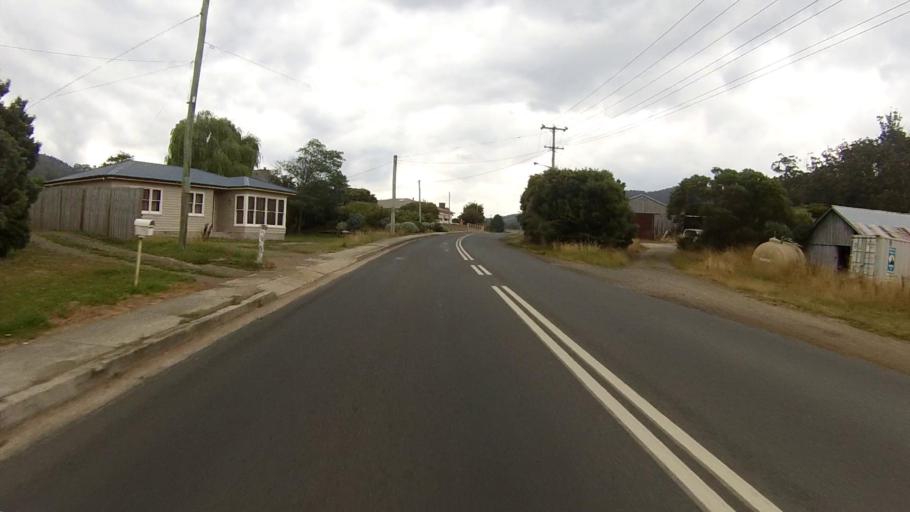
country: AU
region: Tasmania
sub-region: Huon Valley
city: Cygnet
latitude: -43.1529
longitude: 147.0716
